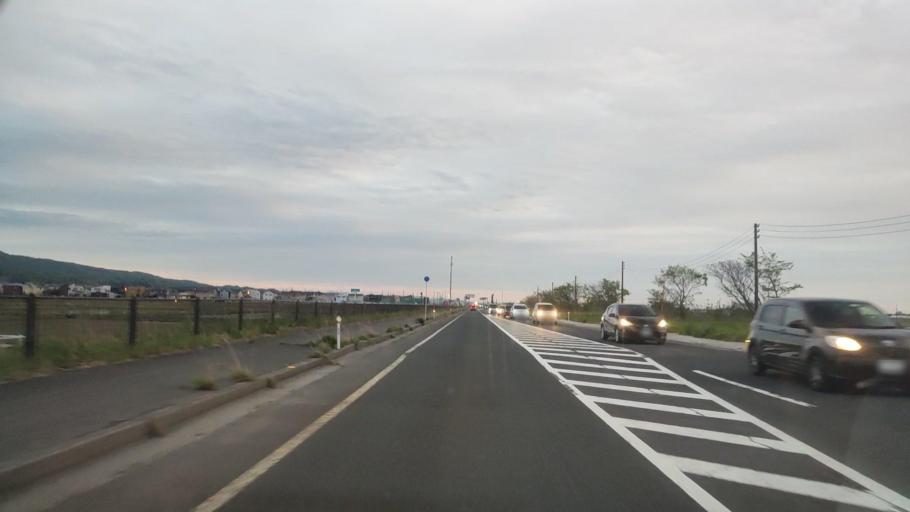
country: JP
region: Niigata
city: Niitsu-honcho
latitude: 37.7559
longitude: 139.0913
